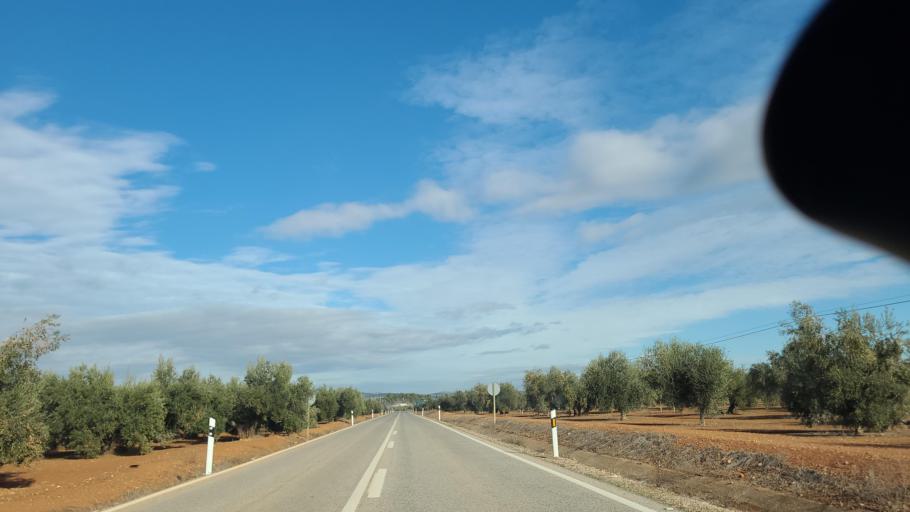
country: ES
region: Andalusia
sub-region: Provincia de Jaen
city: Espeluy
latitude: 38.0253
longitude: -3.8723
